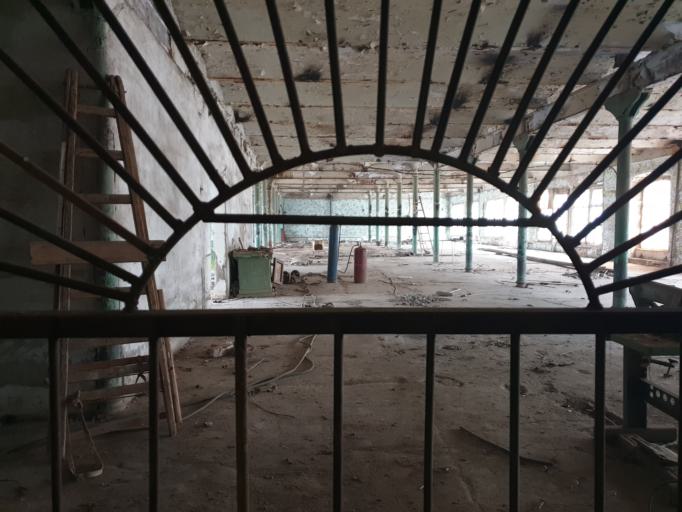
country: RU
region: Kostroma
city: Nerekhta
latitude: 57.4631
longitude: 40.5825
